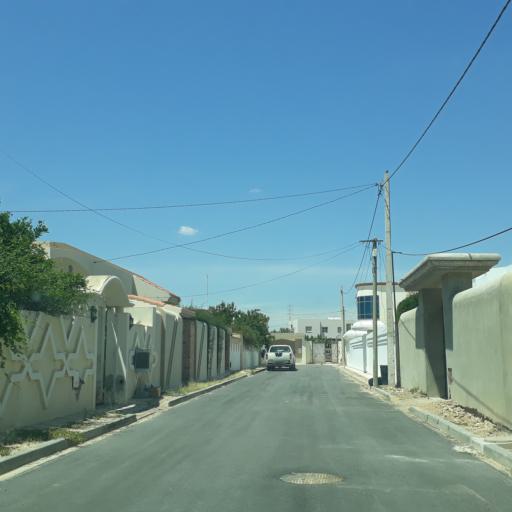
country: TN
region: Safaqis
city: Al Qarmadah
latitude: 34.8154
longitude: 10.7588
